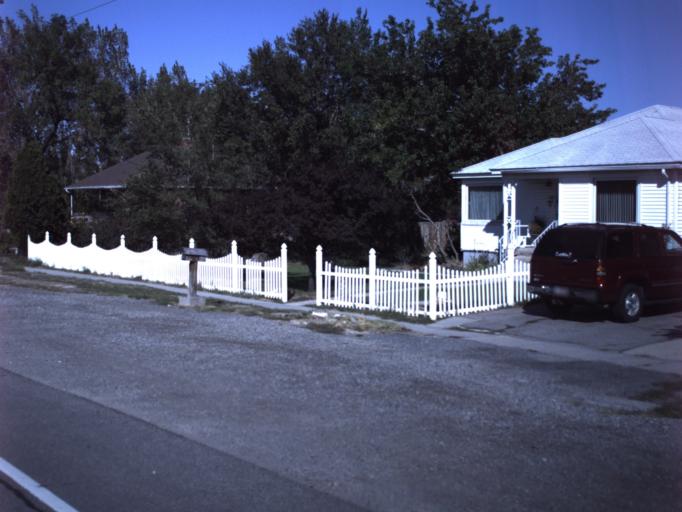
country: US
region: Utah
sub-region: Tooele County
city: Grantsville
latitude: 40.5996
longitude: -112.4281
